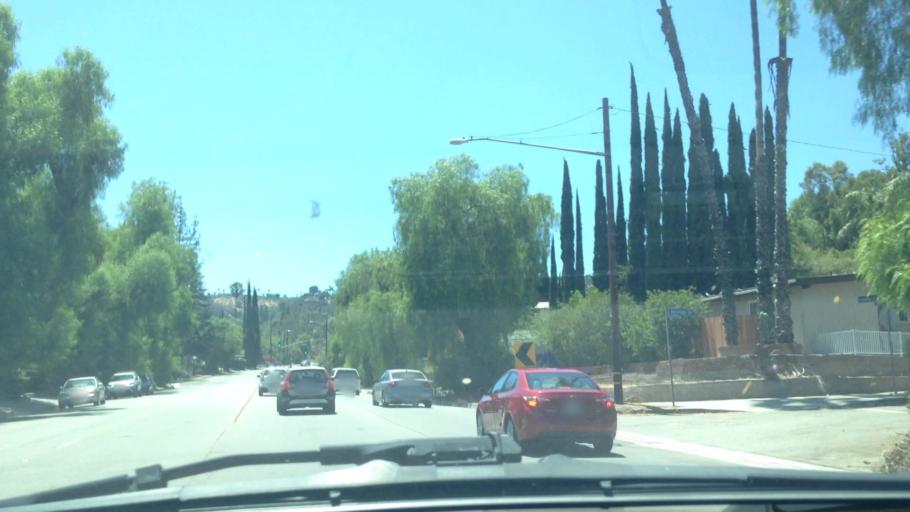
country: US
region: California
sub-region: Los Angeles County
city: Woodland Hills
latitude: 34.1534
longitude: -118.6058
